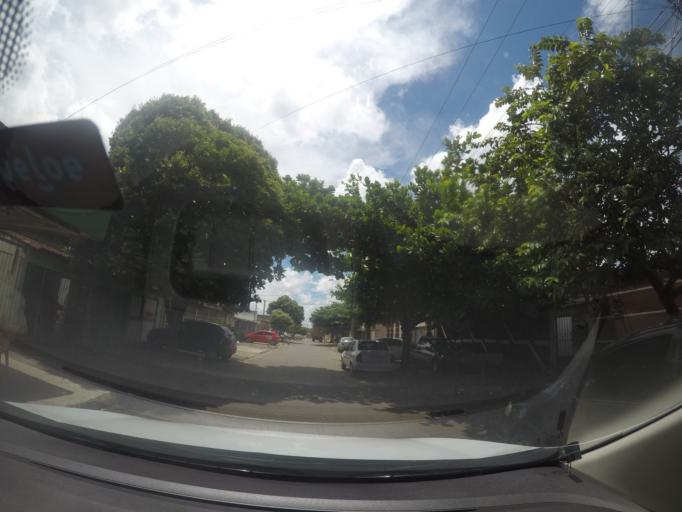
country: BR
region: Goias
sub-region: Goiania
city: Goiania
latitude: -16.6758
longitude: -49.3130
